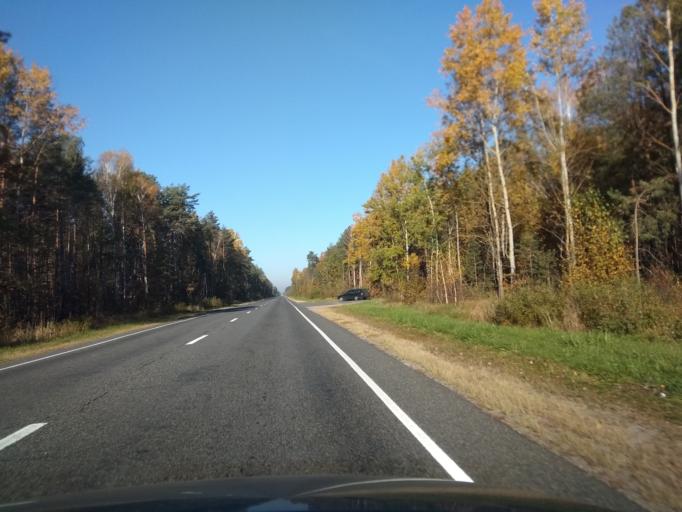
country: BY
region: Brest
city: Malaryta
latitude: 51.9014
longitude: 24.1213
